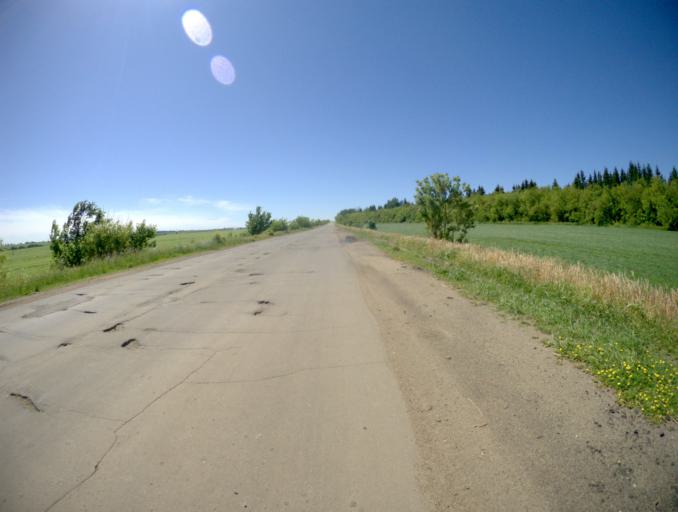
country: RU
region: Ivanovo
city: Gavrilov Posad
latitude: 56.5652
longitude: 40.0440
